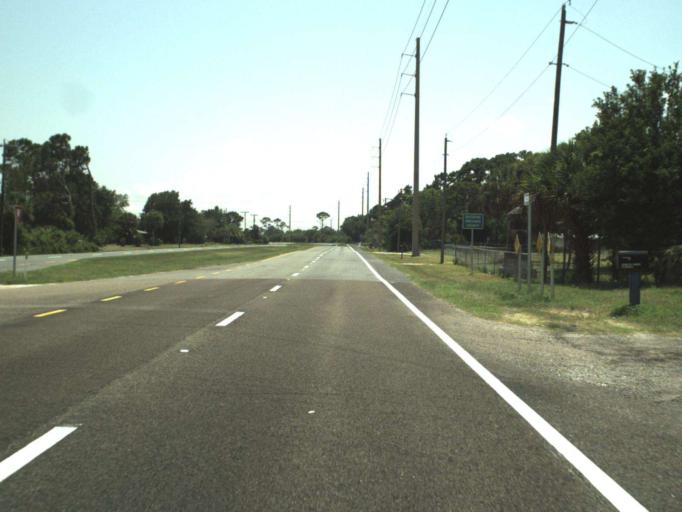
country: US
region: Florida
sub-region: Volusia County
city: Oak Hill
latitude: 28.7914
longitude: -80.8827
